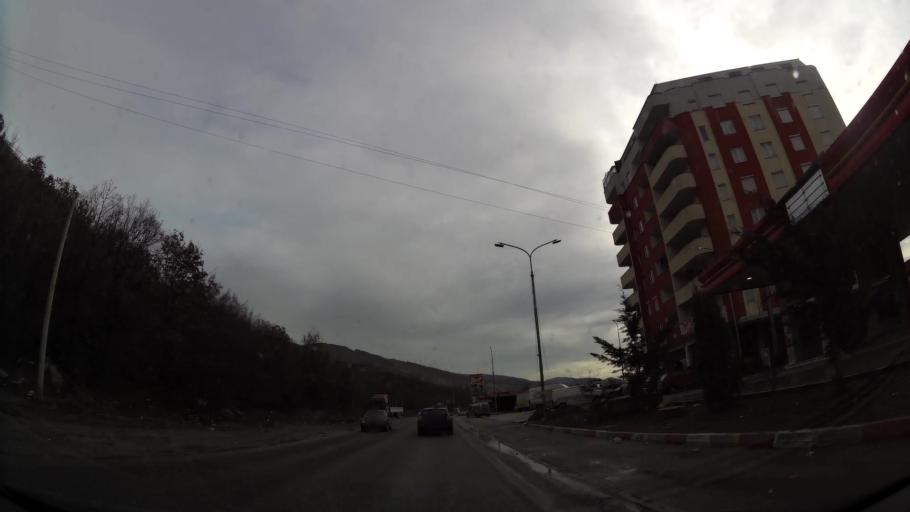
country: XK
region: Ferizaj
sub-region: Hani i Elezit
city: Hani i Elezit
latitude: 42.1558
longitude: 21.2944
